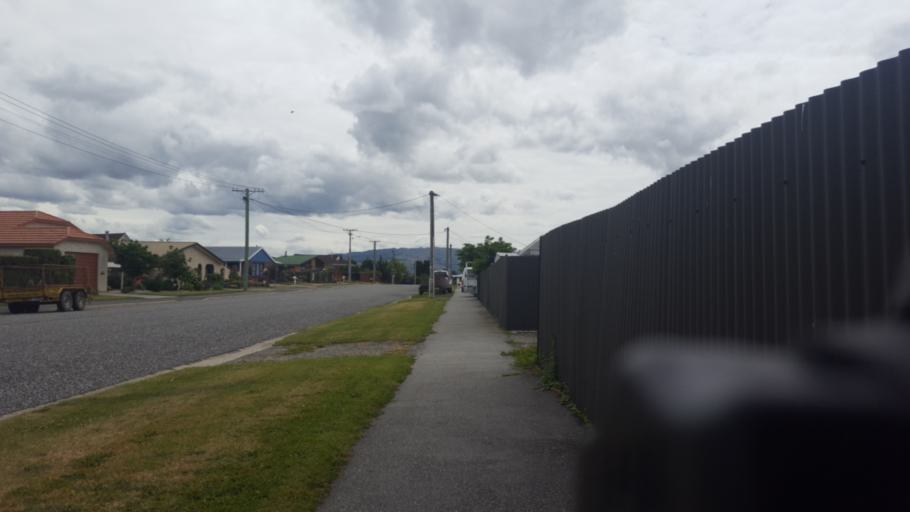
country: NZ
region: Otago
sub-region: Queenstown-Lakes District
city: Wanaka
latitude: -45.2524
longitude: 169.3854
